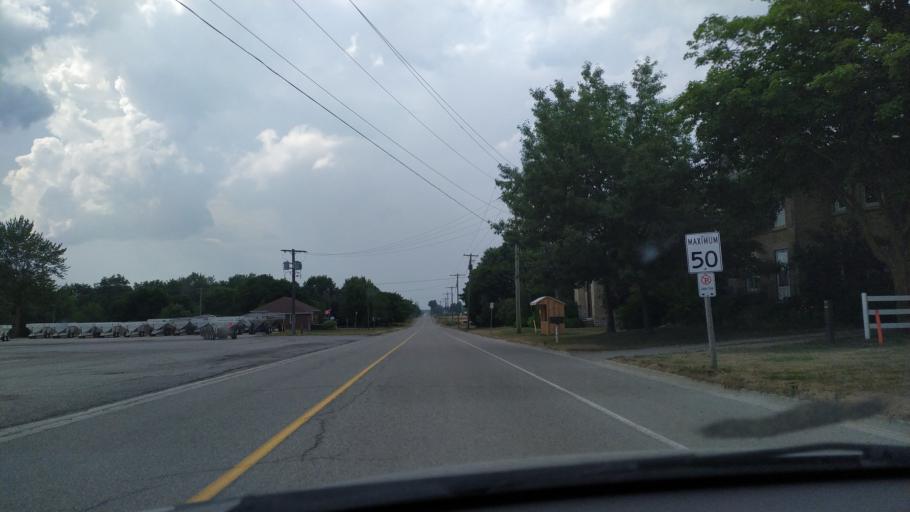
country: CA
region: Ontario
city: Dorchester
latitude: 43.1923
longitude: -81.1484
